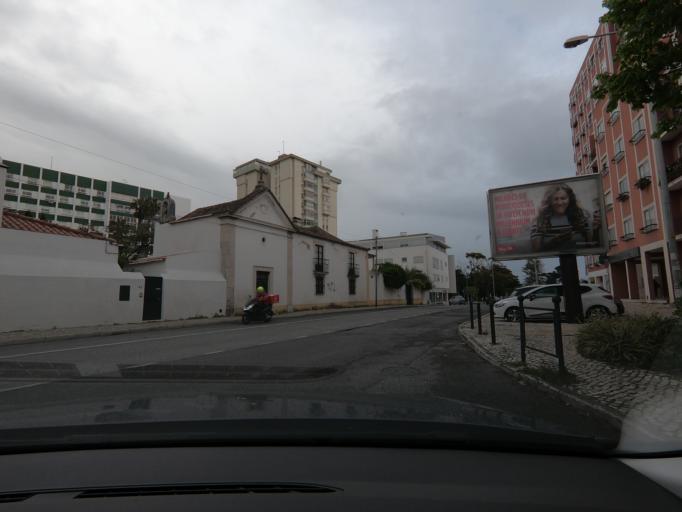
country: PT
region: Lisbon
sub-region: Cascais
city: Sao Domingos de Rana
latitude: 38.6969
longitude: -9.3297
